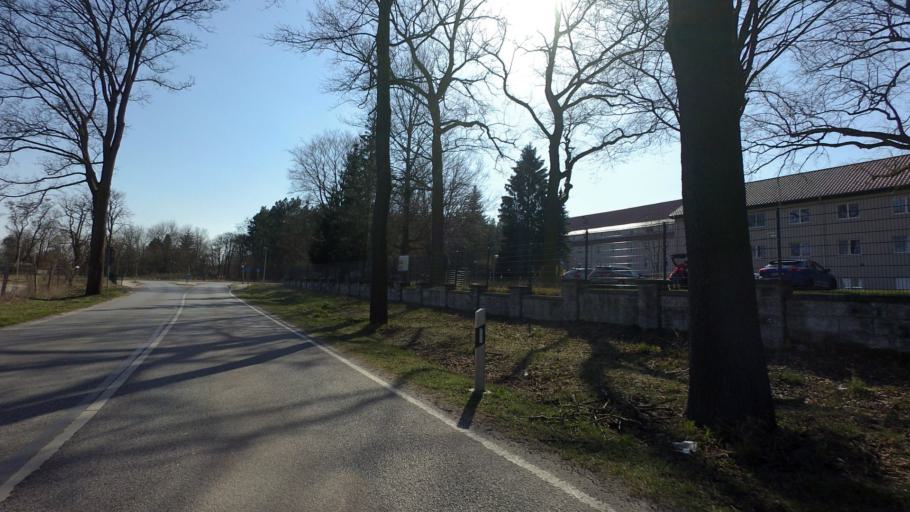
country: DE
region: Brandenburg
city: Leegebruch
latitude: 52.7251
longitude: 13.1792
